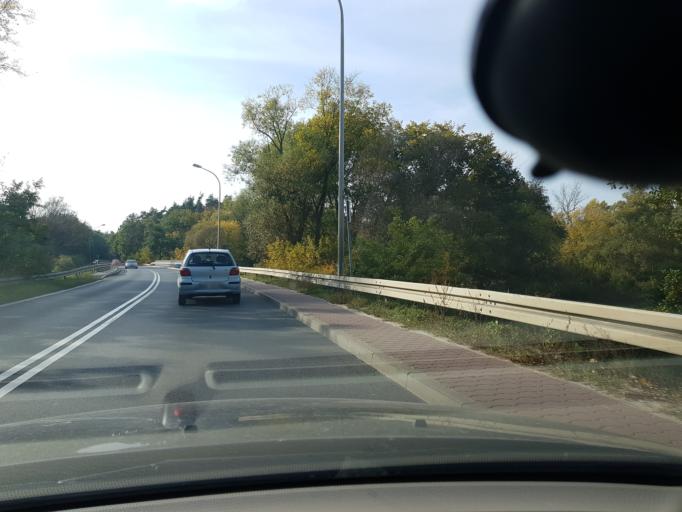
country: PL
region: Masovian Voivodeship
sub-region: Powiat otwocki
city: Jozefow
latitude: 52.1066
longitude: 21.2297
